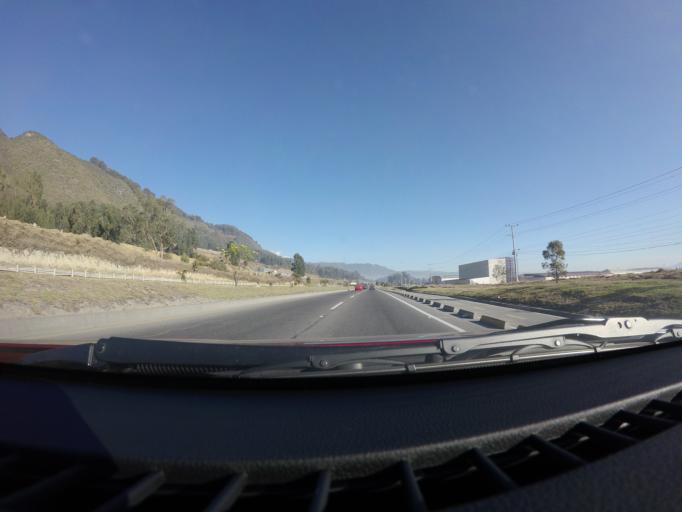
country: CO
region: Cundinamarca
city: Zipaquira
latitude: 4.9829
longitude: -74.0037
